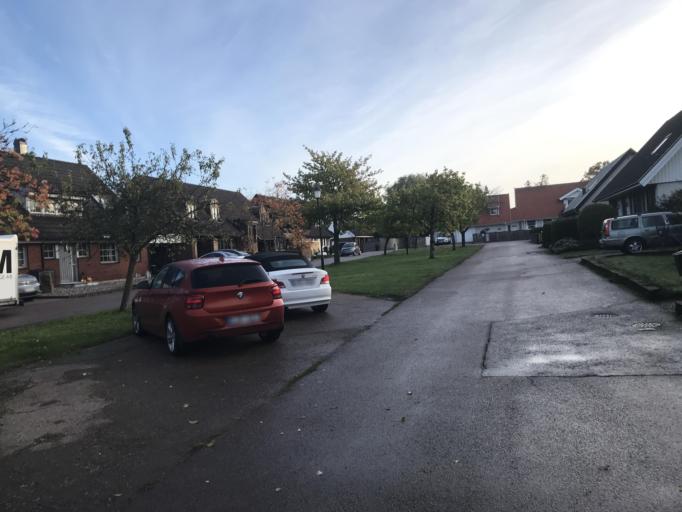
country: SE
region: Skane
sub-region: Landskrona
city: Landskrona
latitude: 55.8858
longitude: 12.8153
